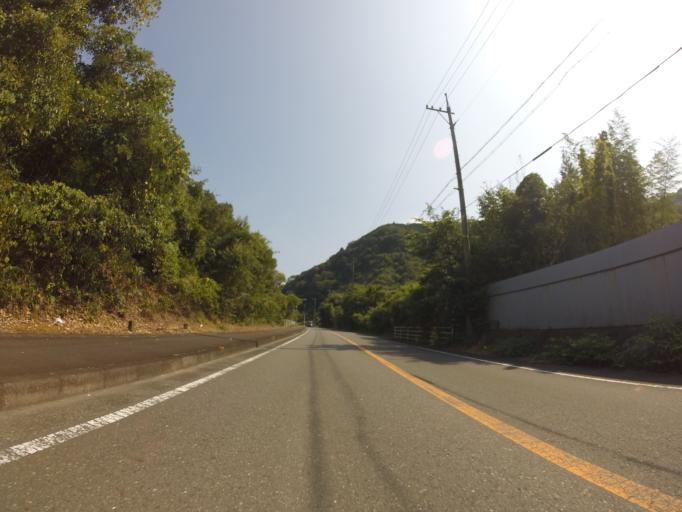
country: JP
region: Shizuoka
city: Shizuoka-shi
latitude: 35.0573
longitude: 138.3637
